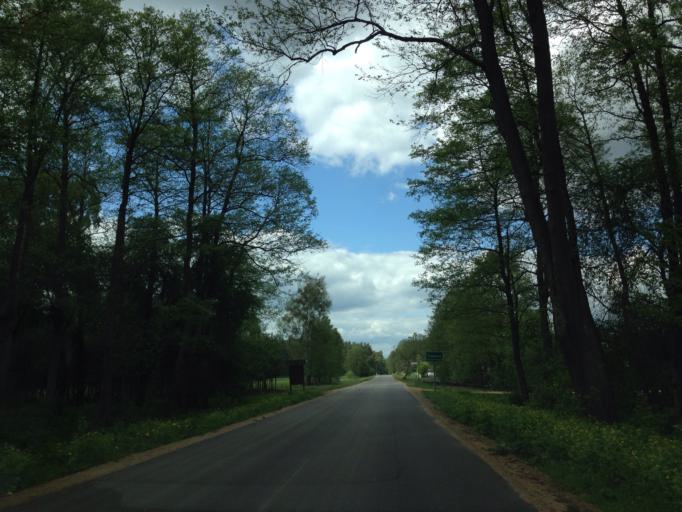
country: PL
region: Podlasie
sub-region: Powiat grajewski
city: Radzilow
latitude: 53.3681
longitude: 22.5927
